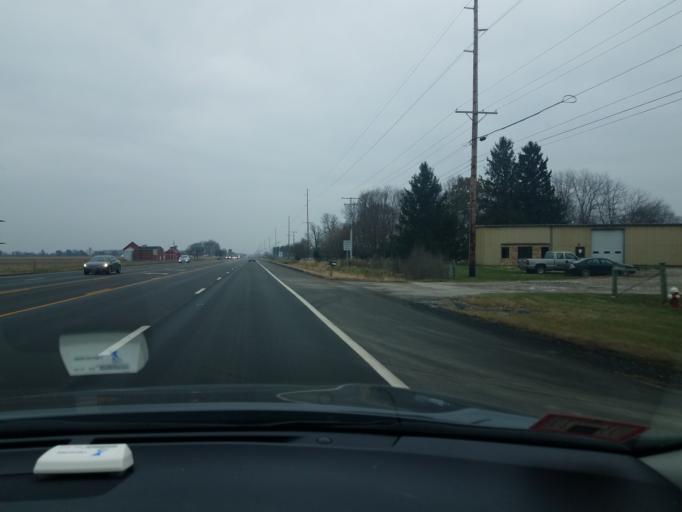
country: US
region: Ohio
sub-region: Erie County
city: Milan
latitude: 41.3754
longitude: -82.6430
